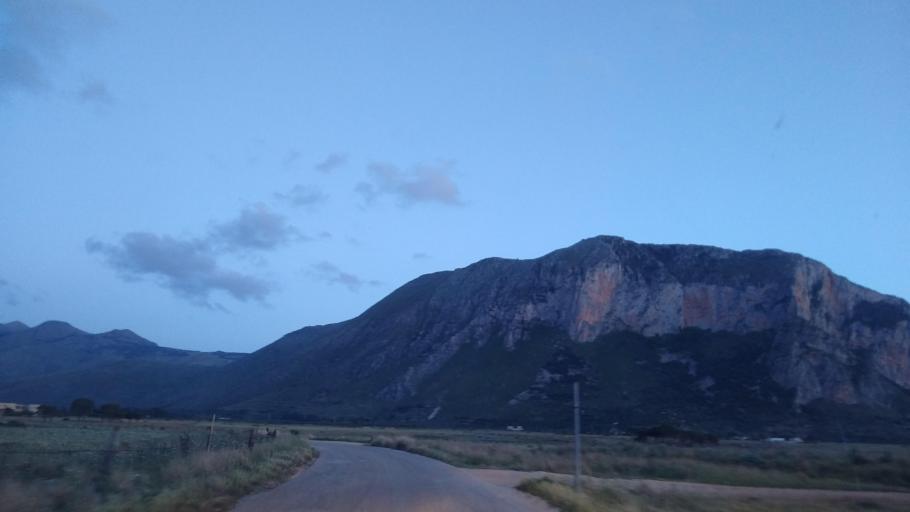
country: IT
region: Sicily
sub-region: Trapani
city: Castelluzzo
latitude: 38.1145
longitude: 12.7202
